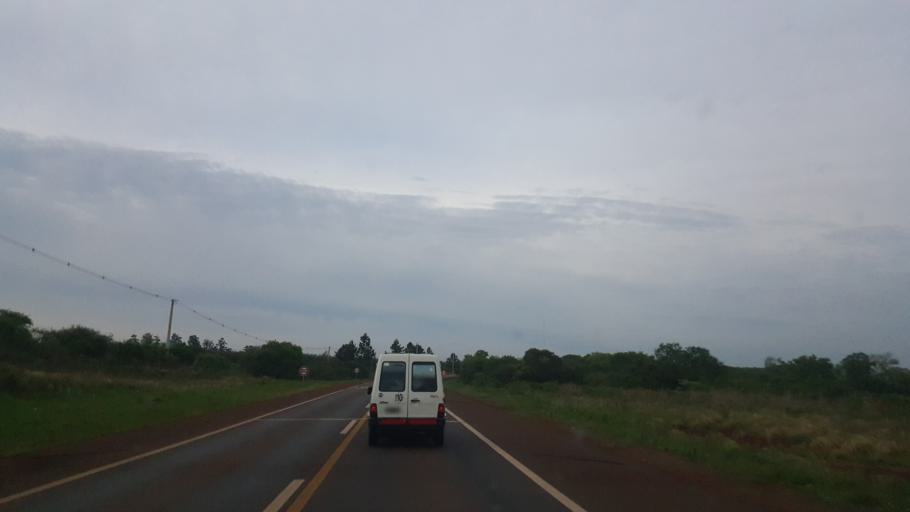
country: AR
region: Misiones
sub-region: Departamento de Apostoles
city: San Jose
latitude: -27.7772
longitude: -55.8105
